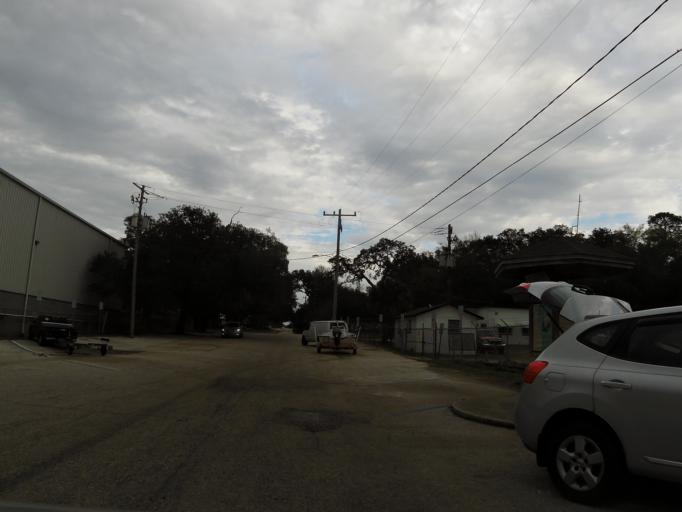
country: US
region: Florida
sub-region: Duval County
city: Jacksonville
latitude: 30.3339
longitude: -81.6118
